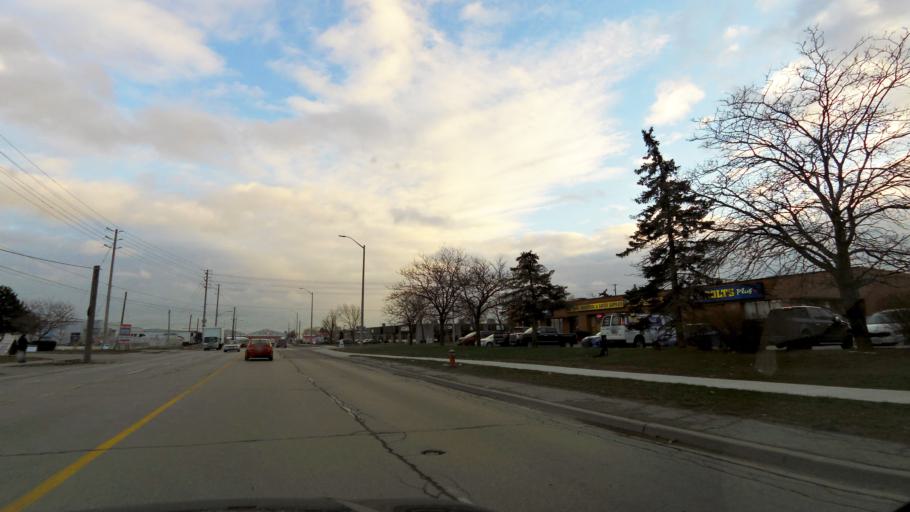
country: CA
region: Ontario
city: Etobicoke
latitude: 43.6965
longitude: -79.6559
